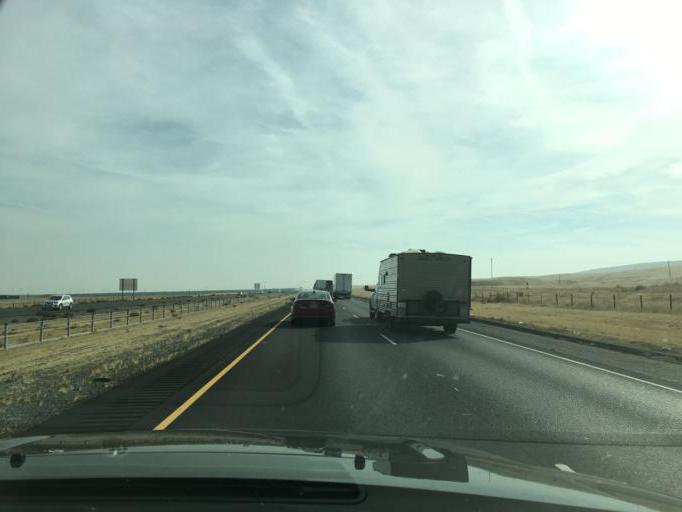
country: US
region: California
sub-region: Kings County
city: Avenal
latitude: 36.0683
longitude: -120.0882
